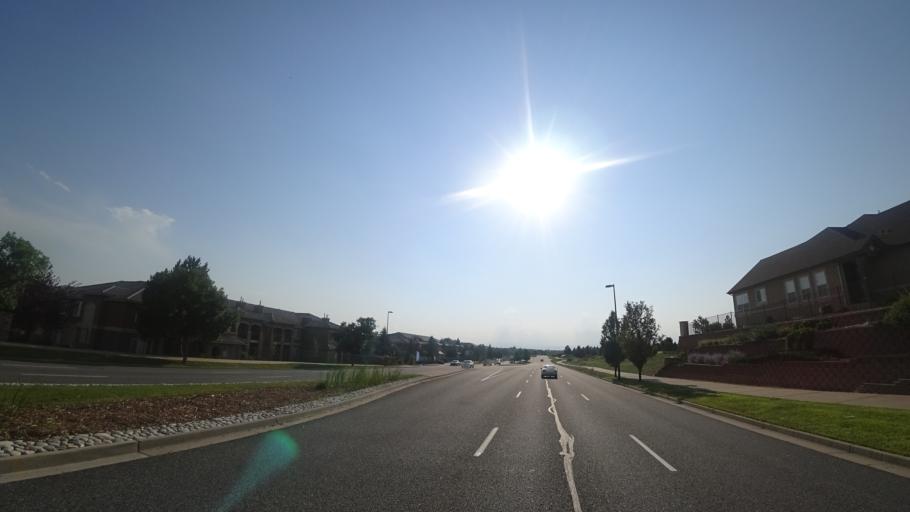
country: US
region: Colorado
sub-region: Douglas County
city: Parker
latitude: 39.5951
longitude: -104.7320
